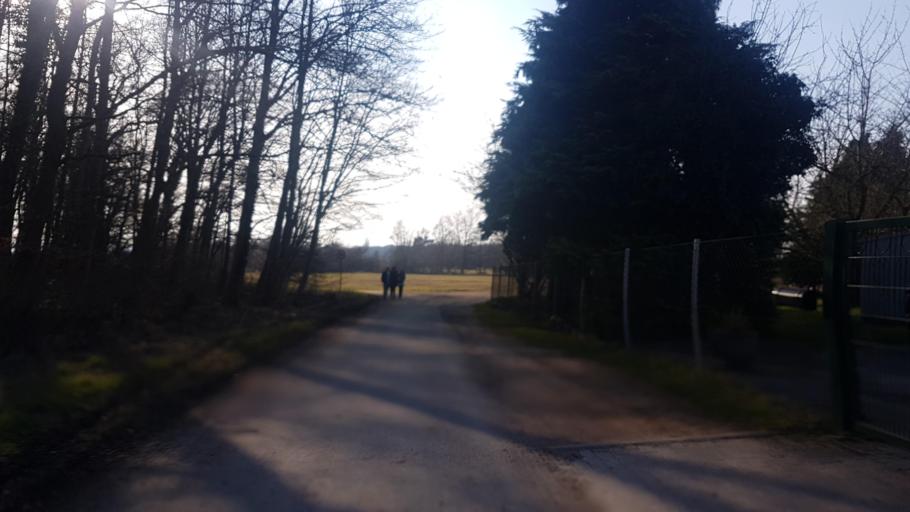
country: DE
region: Lower Saxony
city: Hemmingen
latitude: 52.3153
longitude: 9.6940
